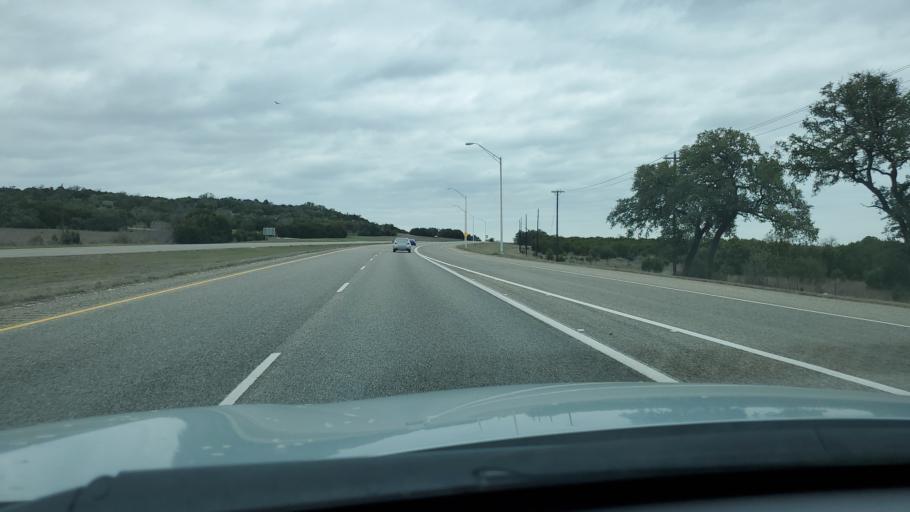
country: US
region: Texas
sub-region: Williamson County
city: Florence
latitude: 30.8829
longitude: -97.8007
